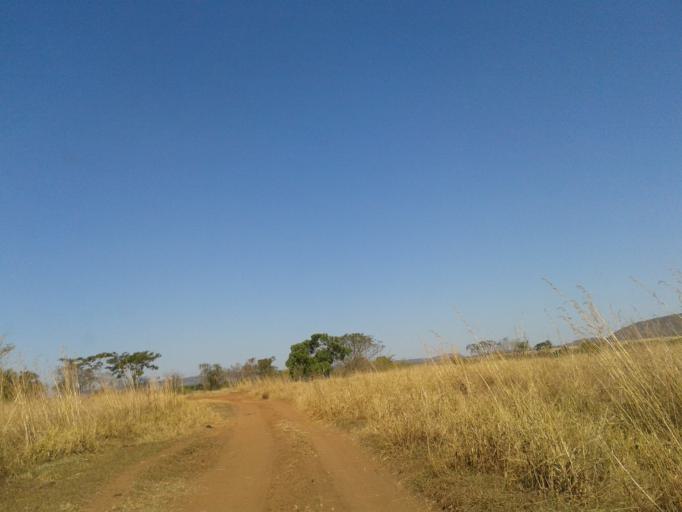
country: BR
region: Minas Gerais
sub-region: Santa Vitoria
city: Santa Vitoria
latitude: -19.1603
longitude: -50.0208
